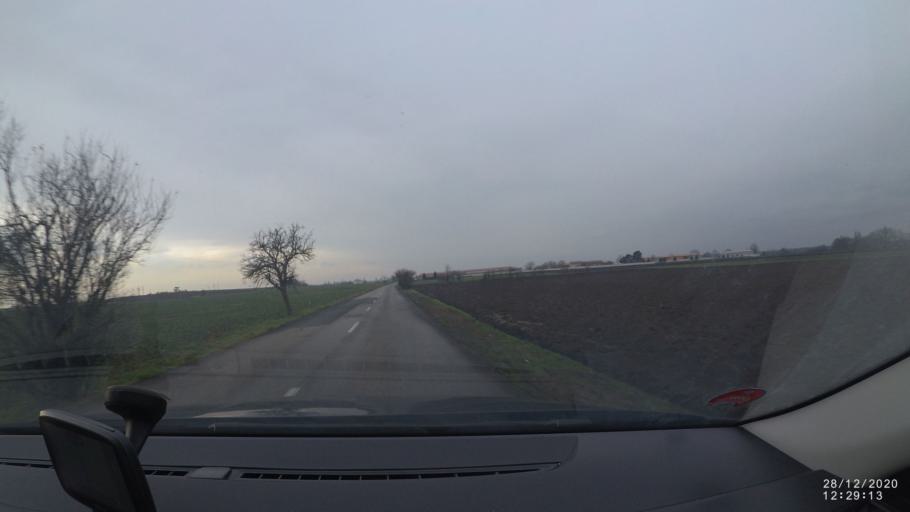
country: CZ
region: Central Bohemia
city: Kostelec nad Labem
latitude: 50.1965
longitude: 14.6187
